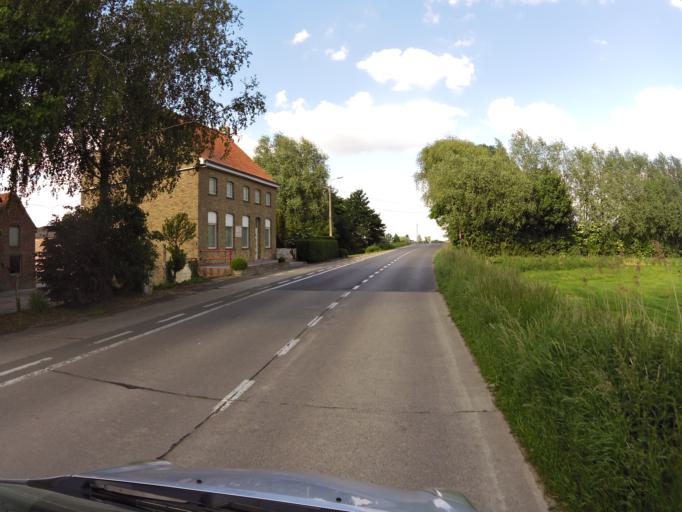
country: BE
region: Flanders
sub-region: Provincie West-Vlaanderen
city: Diksmuide
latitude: 50.9587
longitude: 2.8217
